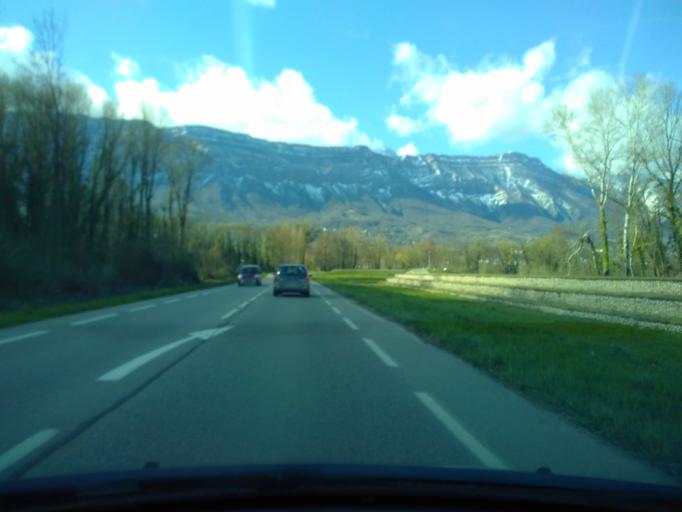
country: FR
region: Rhone-Alpes
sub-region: Departement de l'Isere
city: Domene
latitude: 45.2164
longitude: 5.8243
